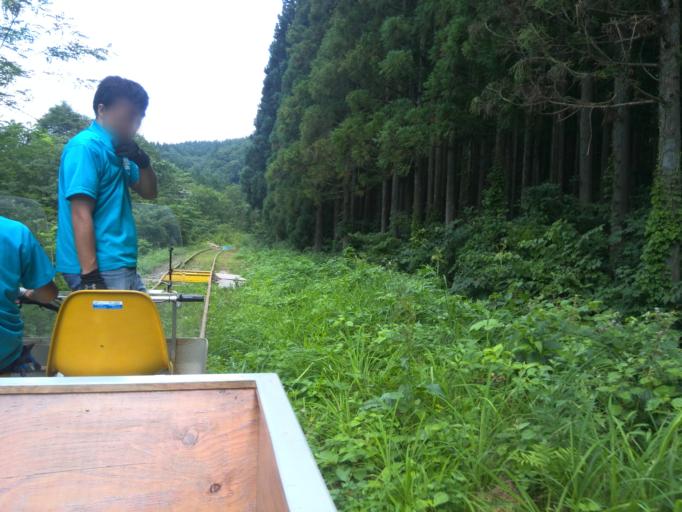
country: JP
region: Akita
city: Odate
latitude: 40.2974
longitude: 140.6472
